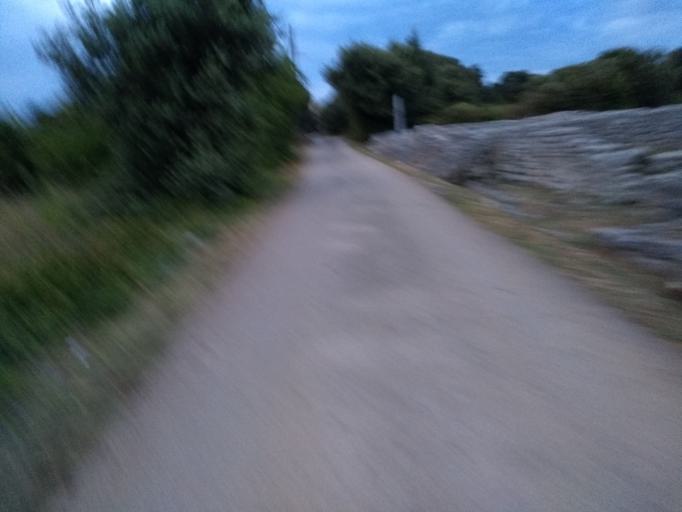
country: HR
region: Zadarska
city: Ugljan
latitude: 44.1397
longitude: 15.0723
